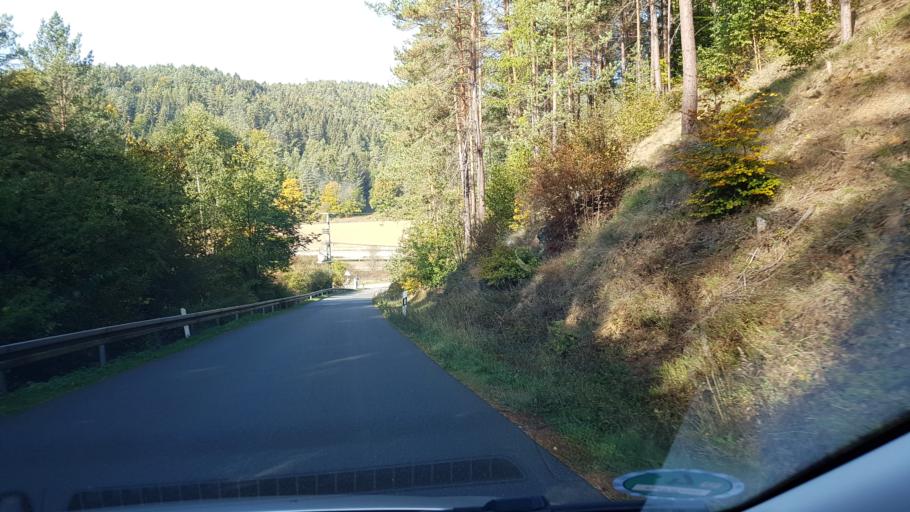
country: DE
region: Bavaria
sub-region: Upper Franconia
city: Waischenfeld
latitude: 49.8278
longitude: 11.3322
